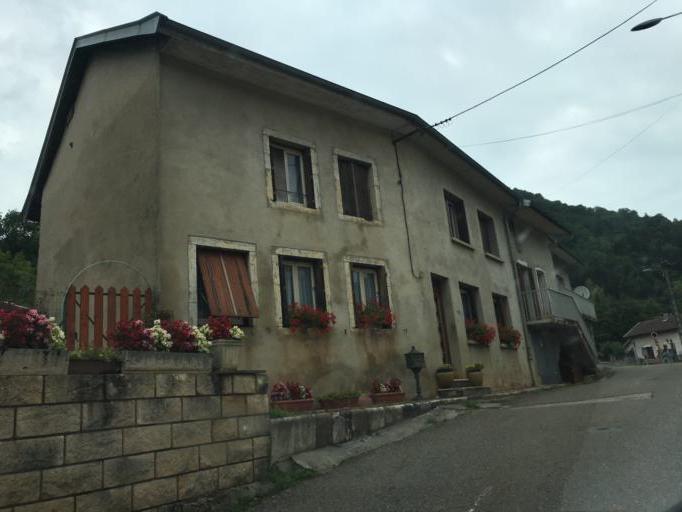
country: FR
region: Franche-Comte
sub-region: Departement du Jura
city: Lavans-les-Saint-Claude
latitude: 46.3601
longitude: 5.7856
